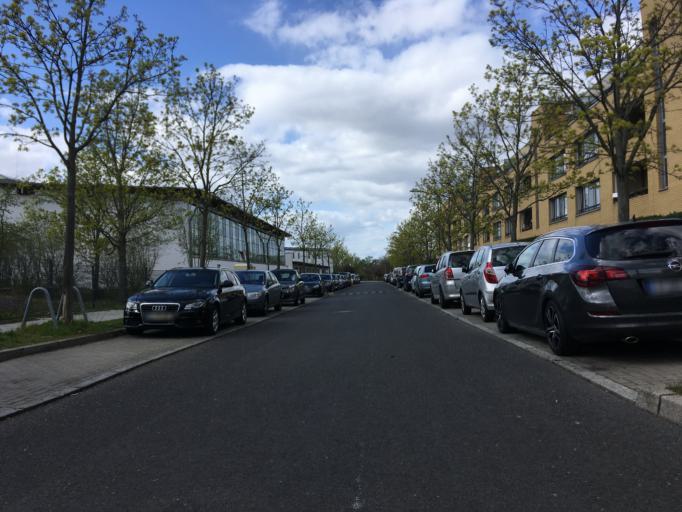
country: DE
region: Berlin
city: Altglienicke
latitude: 52.4063
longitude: 13.5388
